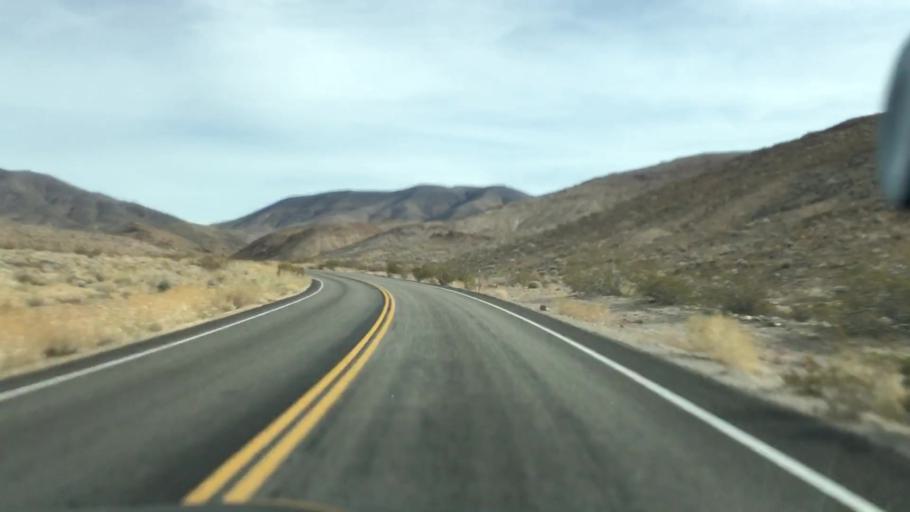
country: US
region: Nevada
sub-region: Nye County
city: Beatty
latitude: 36.7461
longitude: -116.9426
